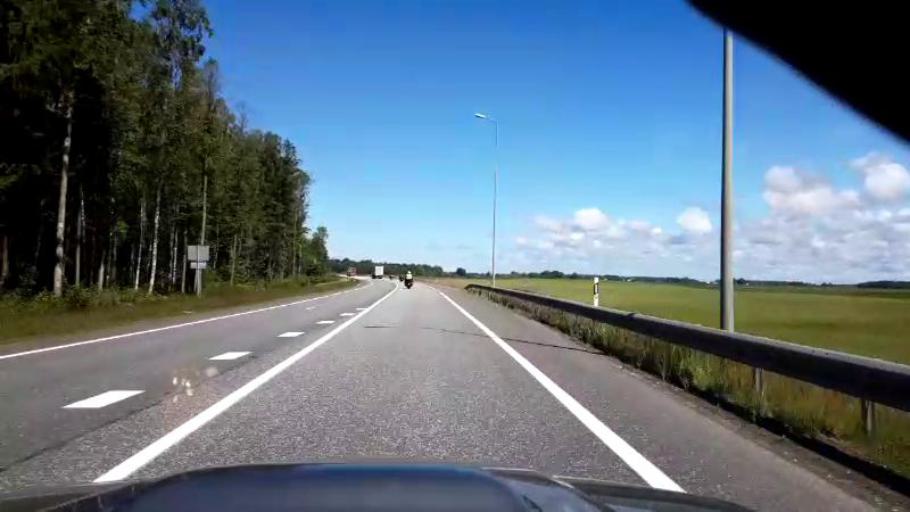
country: LV
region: Saulkrastu
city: Saulkrasti
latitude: 57.4110
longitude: 24.4319
